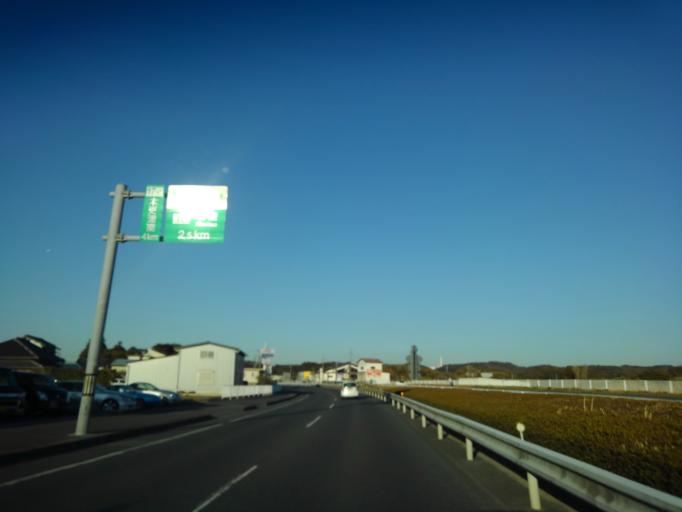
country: JP
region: Chiba
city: Kimitsu
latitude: 35.3124
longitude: 139.9258
